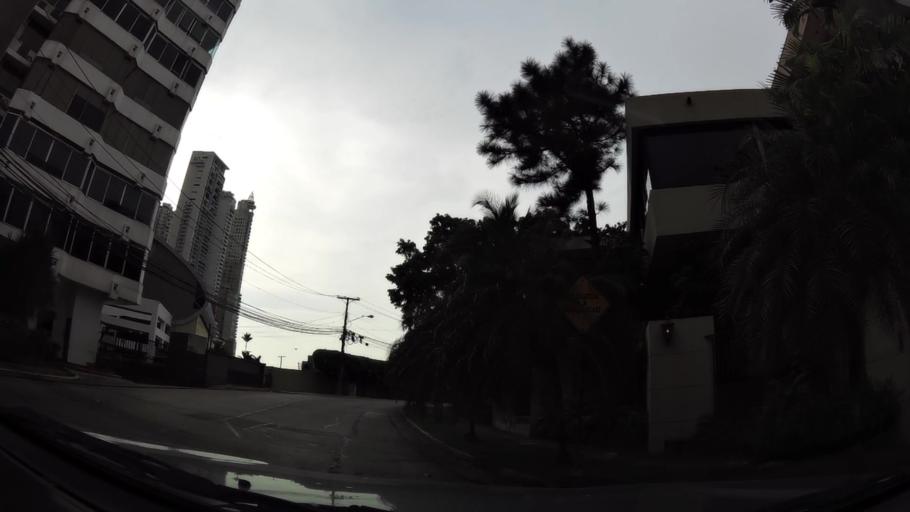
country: PA
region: Panama
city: Panama
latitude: 8.9767
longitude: -79.5107
